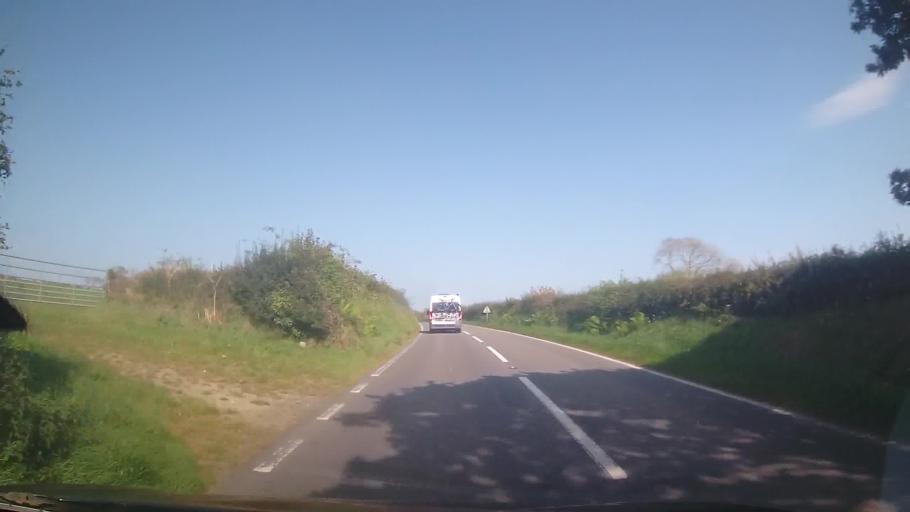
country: GB
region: Wales
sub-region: Pembrokeshire
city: Crymych
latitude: 52.0158
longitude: -4.7050
